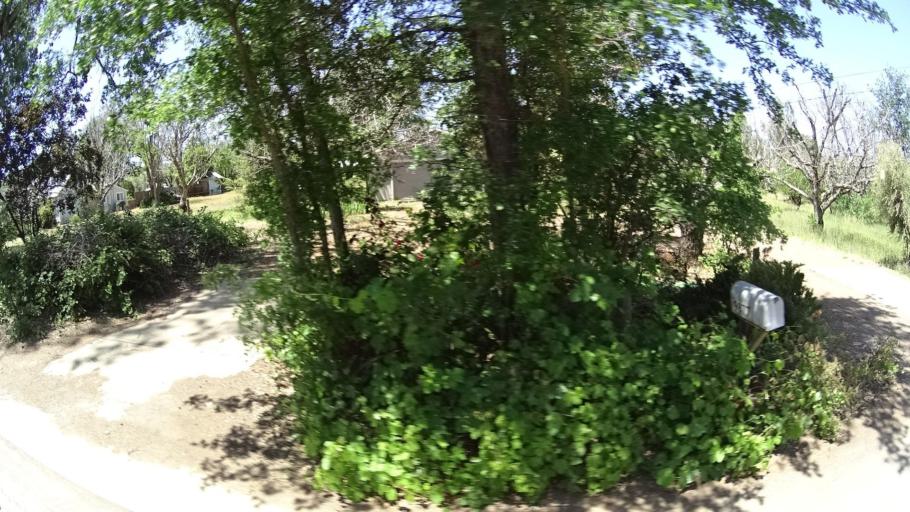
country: US
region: California
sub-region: Lake County
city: Lower Lake
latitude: 38.9108
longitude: -122.5901
